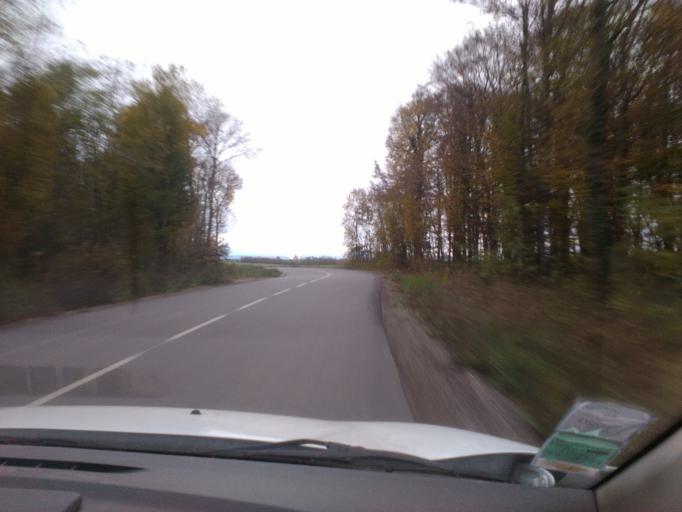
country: FR
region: Lorraine
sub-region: Departement des Vosges
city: Darnieulles
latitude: 48.2316
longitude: 6.3077
